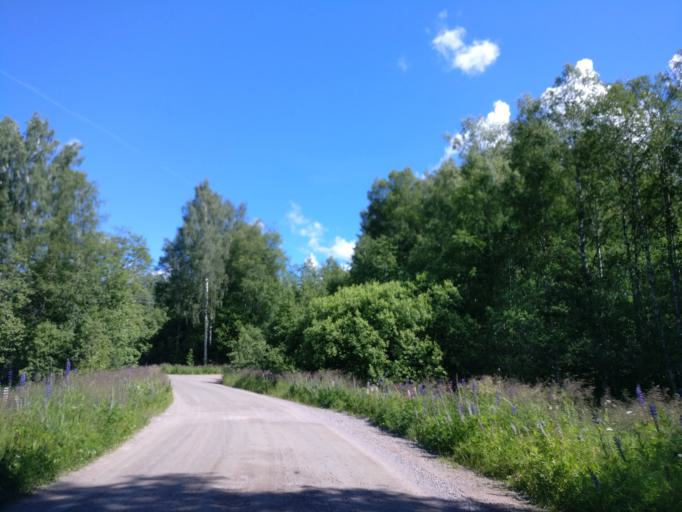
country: SE
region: Vaermland
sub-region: Hagfors Kommun
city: Hagfors
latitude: 60.0384
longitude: 13.6403
